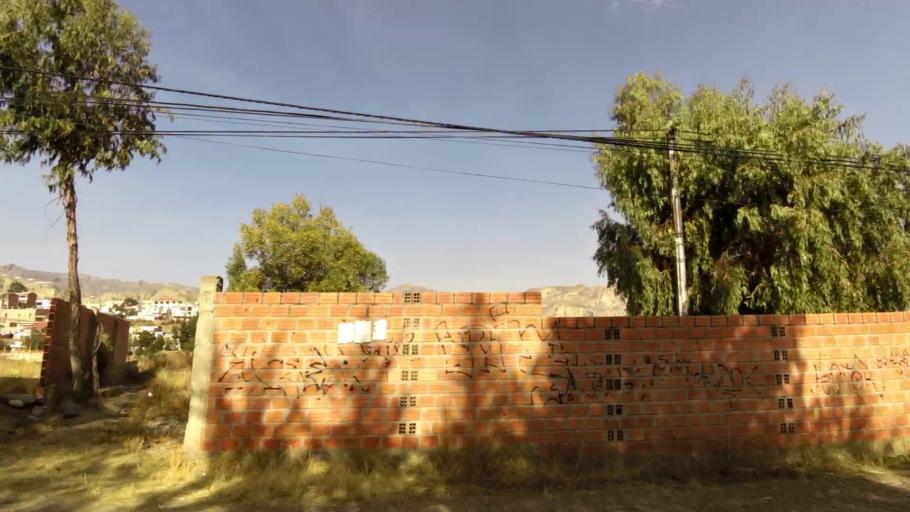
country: BO
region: La Paz
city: La Paz
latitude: -16.5294
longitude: -68.0797
